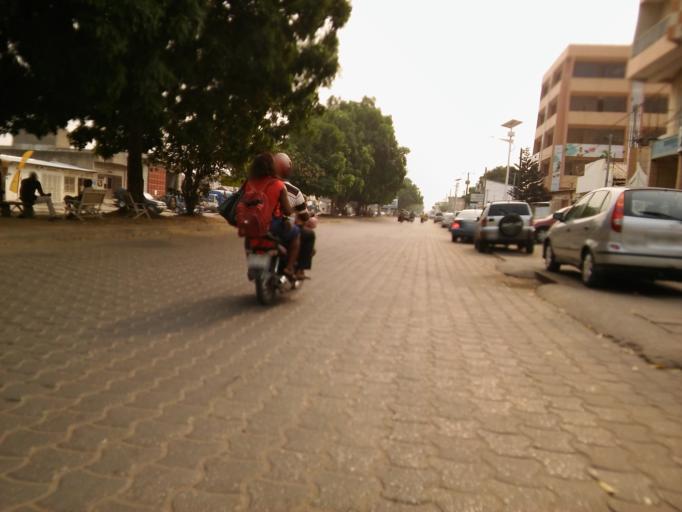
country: BJ
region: Littoral
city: Cotonou
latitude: 6.3813
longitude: 2.4122
